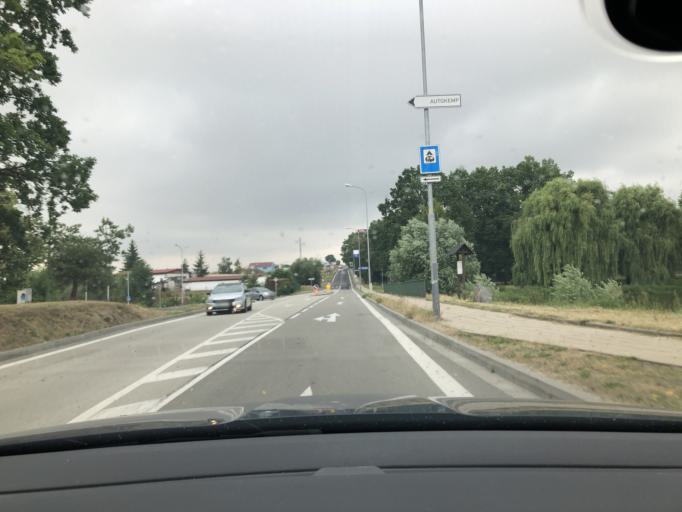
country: CZ
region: Vysocina
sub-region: Okres Trebic
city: Trebic
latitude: 49.2214
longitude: 15.8665
